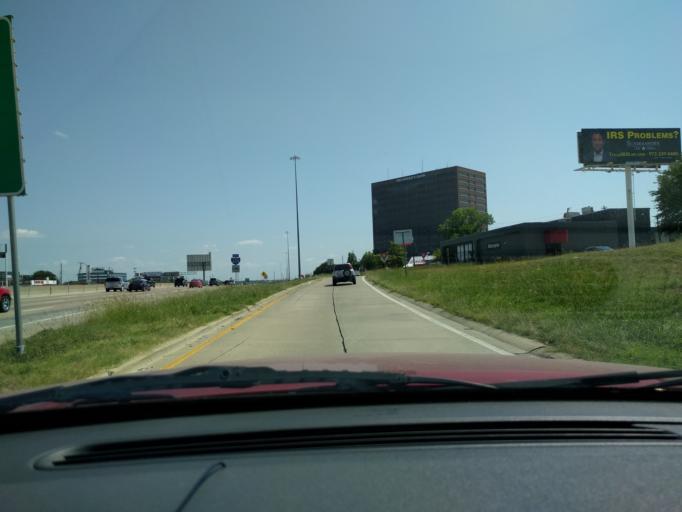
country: US
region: Texas
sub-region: Dallas County
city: Richardson
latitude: 32.9147
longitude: -96.7408
